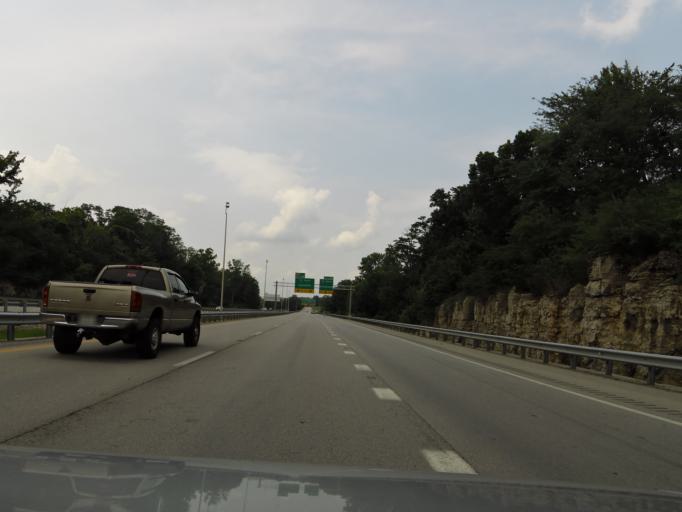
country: US
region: Kentucky
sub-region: Jefferson County
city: Northfield
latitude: 38.2834
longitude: -85.6401
